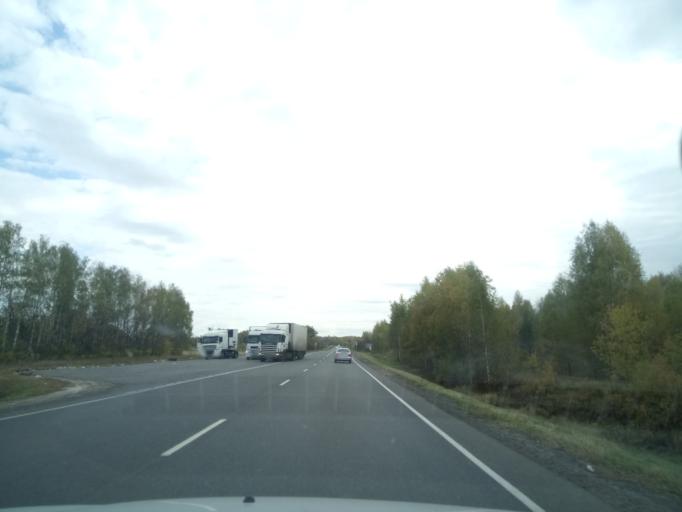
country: RU
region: Nizjnij Novgorod
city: Lukoyanov
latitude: 55.0577
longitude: 44.3657
